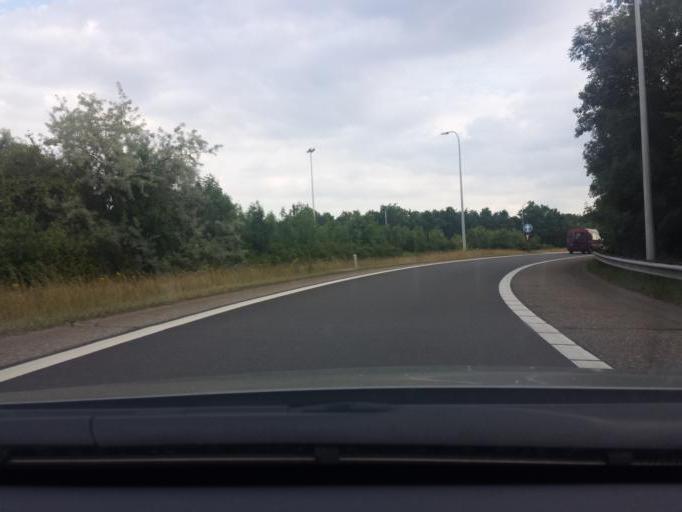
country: BE
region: Flanders
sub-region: Provincie Limburg
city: Halen
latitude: 50.9647
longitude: 5.0825
